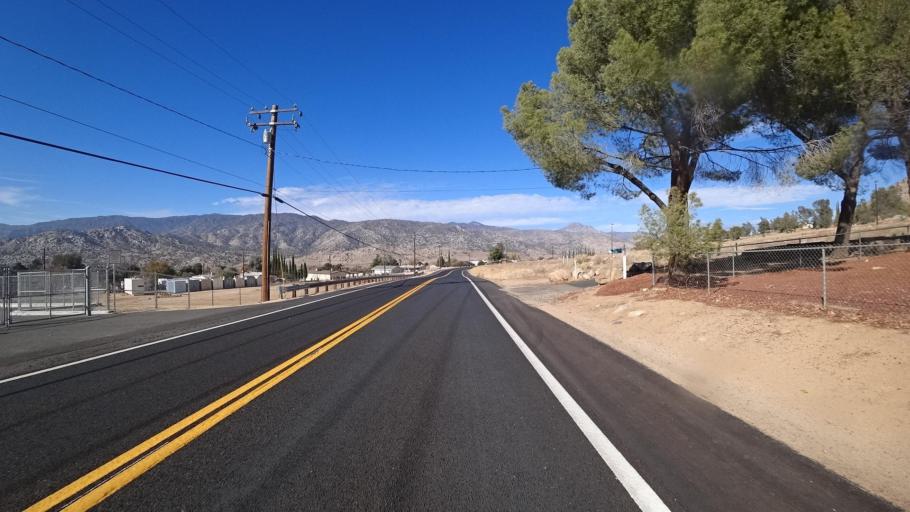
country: US
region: California
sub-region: Kern County
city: Lake Isabella
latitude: 35.6122
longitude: -118.4676
